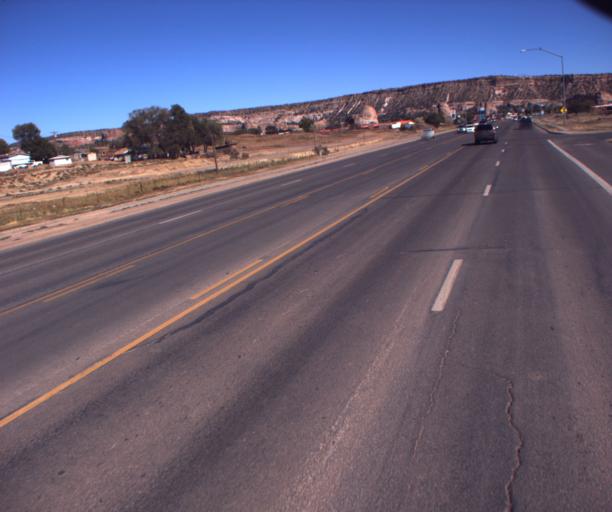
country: US
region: Arizona
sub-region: Apache County
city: Window Rock
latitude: 35.6624
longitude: -109.0625
